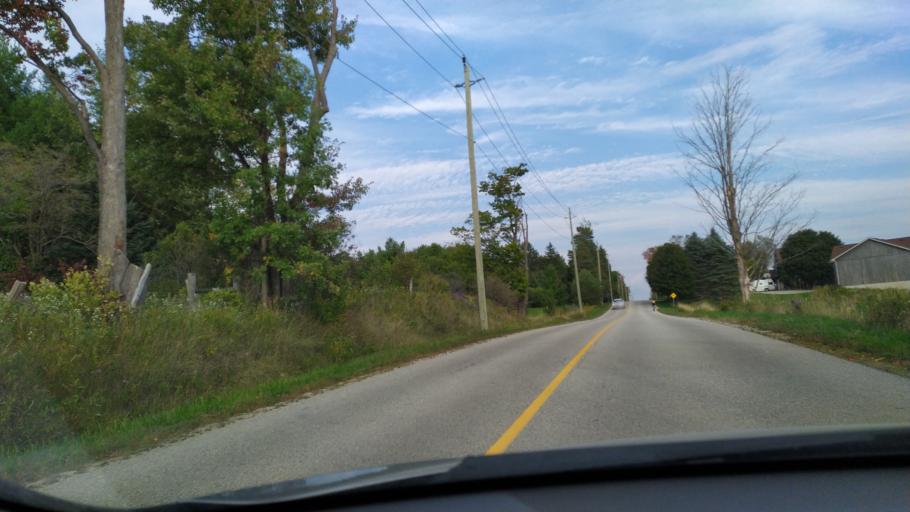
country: CA
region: Ontario
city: Stratford
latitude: 43.4691
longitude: -80.7803
